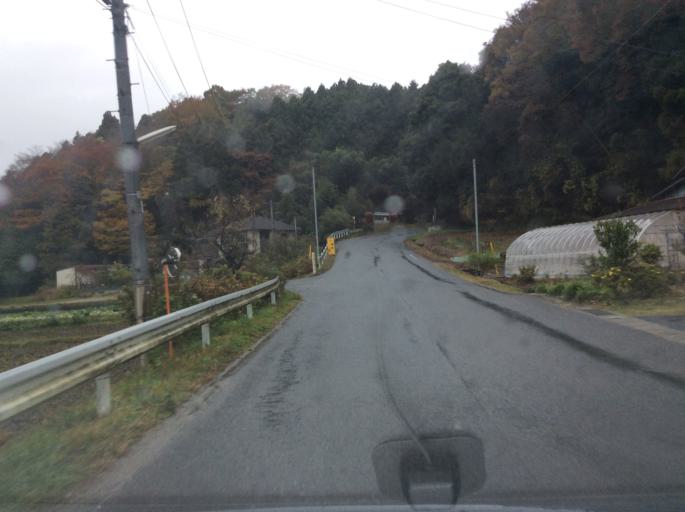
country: JP
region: Fukushima
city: Iwaki
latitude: 37.1055
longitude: 140.9321
